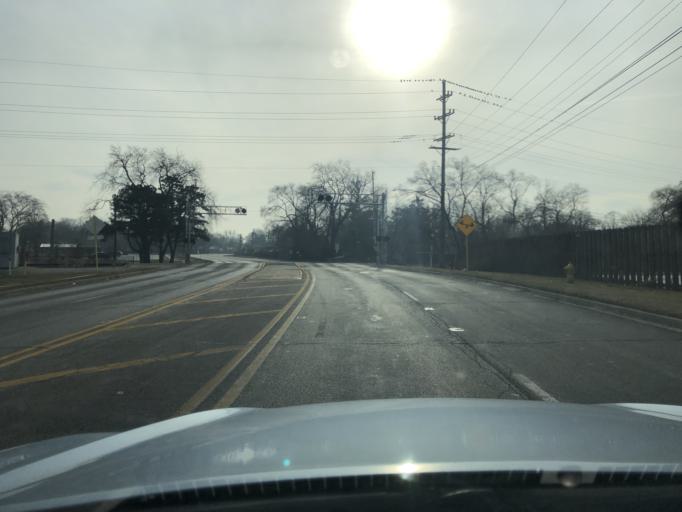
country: US
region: Illinois
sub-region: Cook County
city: Des Plaines
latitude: 42.0424
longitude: -87.9116
